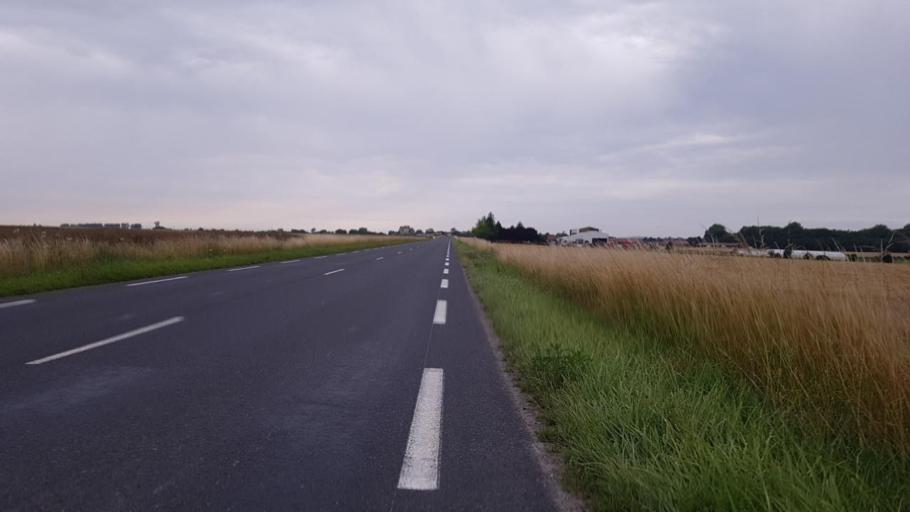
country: FR
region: Champagne-Ardenne
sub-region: Departement de la Marne
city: Pargny-sur-Saulx
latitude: 48.7657
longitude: 4.8210
